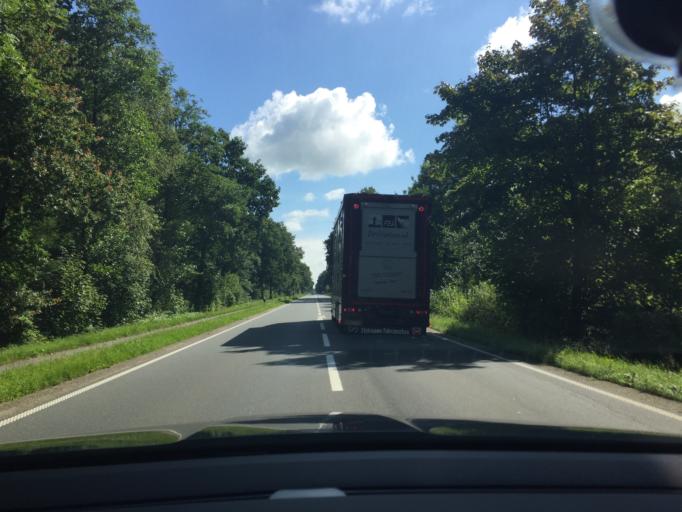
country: DE
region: Lower Saxony
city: Wittmund
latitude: 53.5656
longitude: 7.7300
